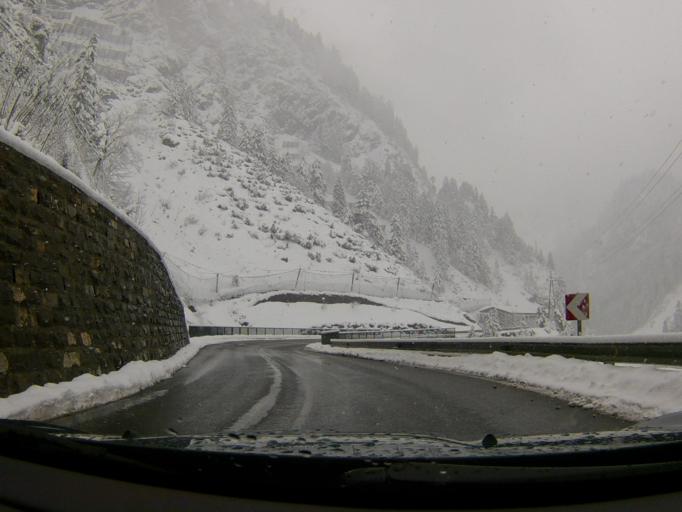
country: AT
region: Vorarlberg
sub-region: Politischer Bezirk Bregenz
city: Schroecken
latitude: 47.2702
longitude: 10.0649
